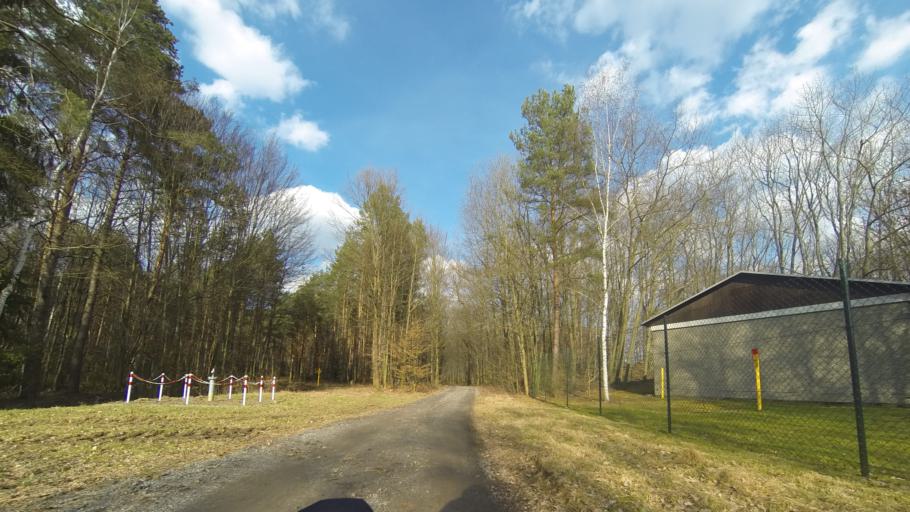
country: DE
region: Saxony
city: Moritzburg
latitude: 51.1528
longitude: 13.6536
